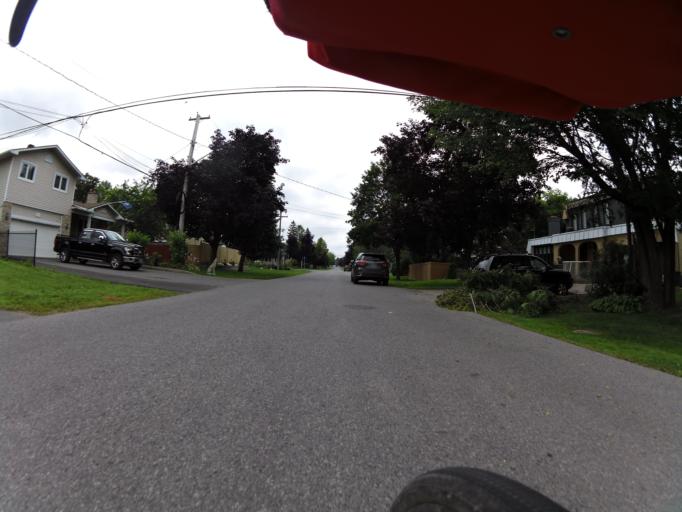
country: CA
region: Ontario
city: Ottawa
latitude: 45.3625
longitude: -75.7049
